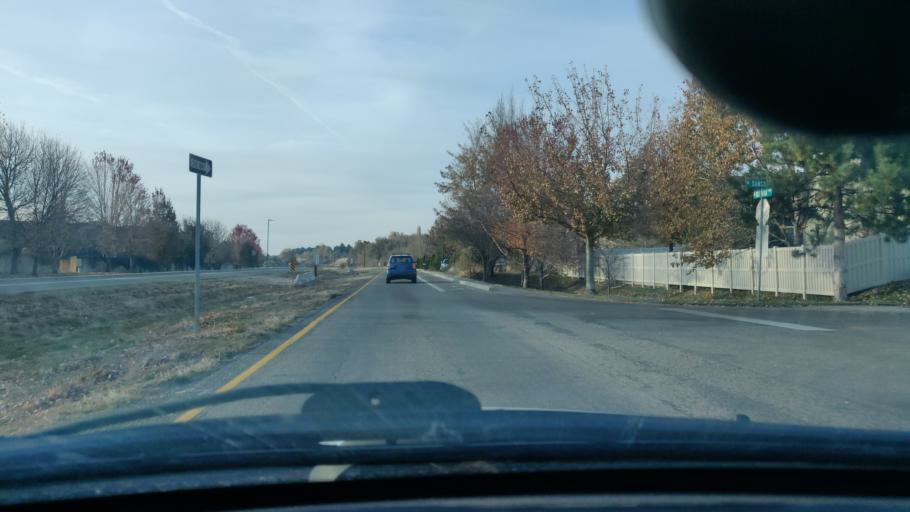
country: US
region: Idaho
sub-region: Ada County
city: Eagle
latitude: 43.6850
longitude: -116.2914
